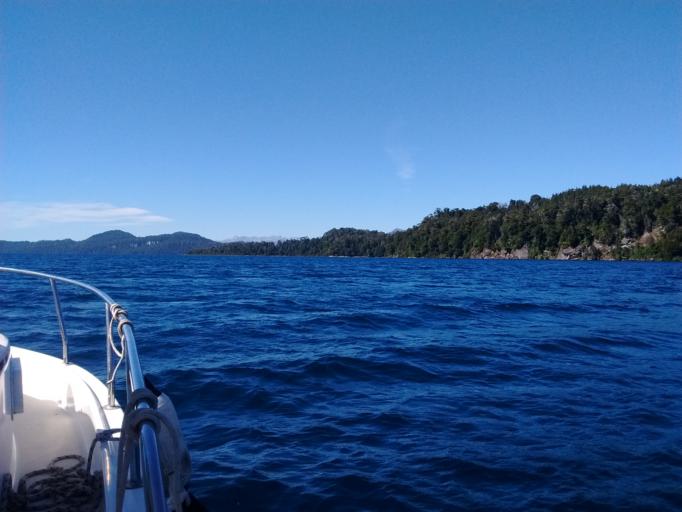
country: AR
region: Neuquen
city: Villa La Angostura
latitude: -40.8250
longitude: -71.6034
